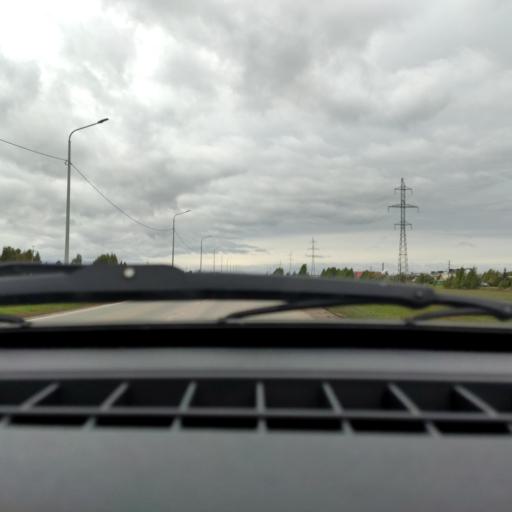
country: RU
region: Bashkortostan
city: Rayevskiy
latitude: 54.0581
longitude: 54.9124
